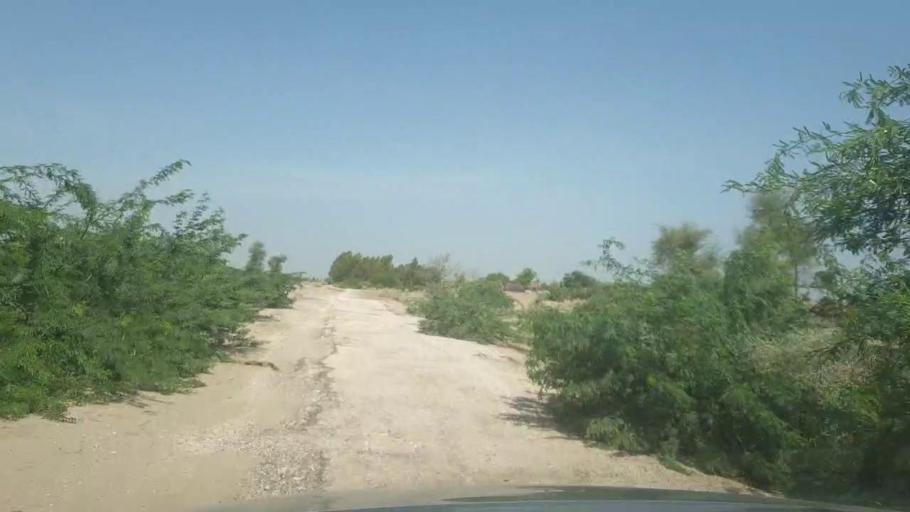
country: PK
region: Sindh
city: Khairpur
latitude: 27.3947
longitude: 69.0743
